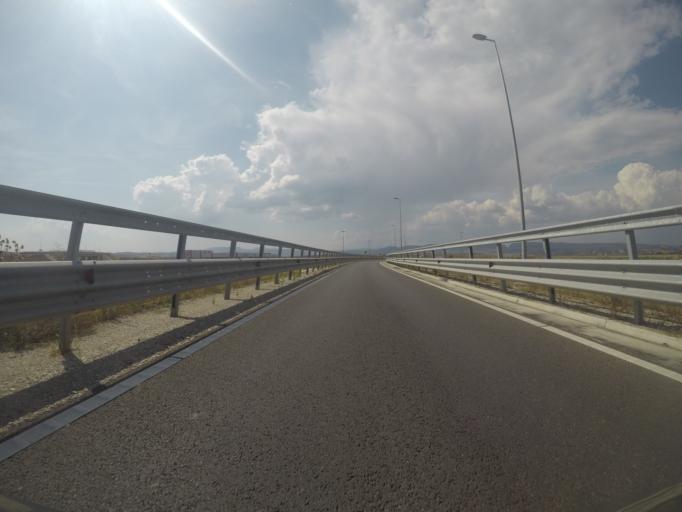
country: RO
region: Cluj
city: Turda
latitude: 46.5281
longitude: 23.7962
